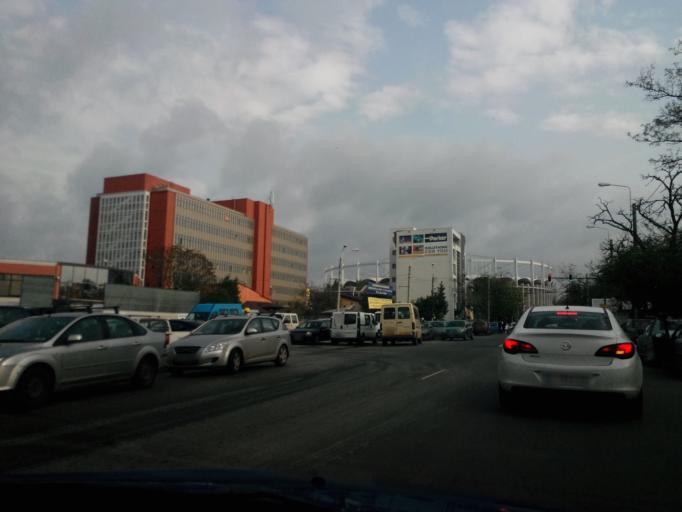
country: RO
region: Ilfov
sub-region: Comuna Fundeni-Dobroesti
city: Fundeni
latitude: 44.4420
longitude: 26.1500
